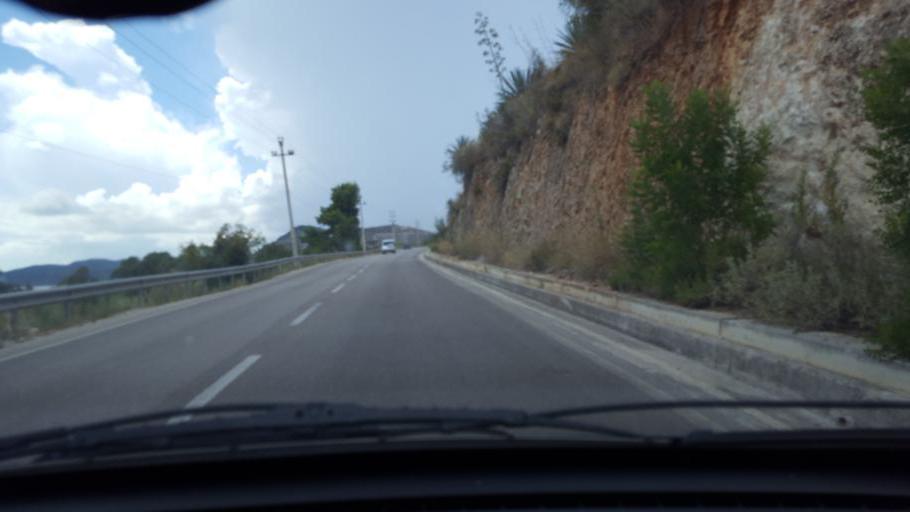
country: AL
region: Vlore
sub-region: Rrethi i Sarandes
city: Sarande
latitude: 39.8205
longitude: 20.0187
